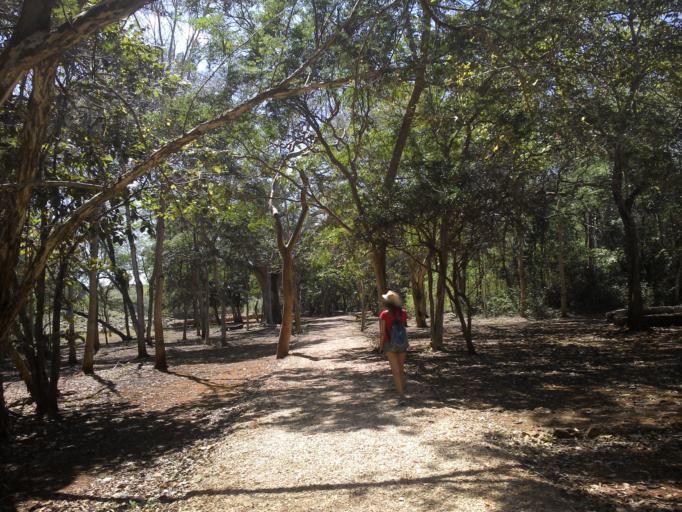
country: MX
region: Yucatan
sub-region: Oxkutzcab
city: Xul
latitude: 20.1741
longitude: -89.5795
